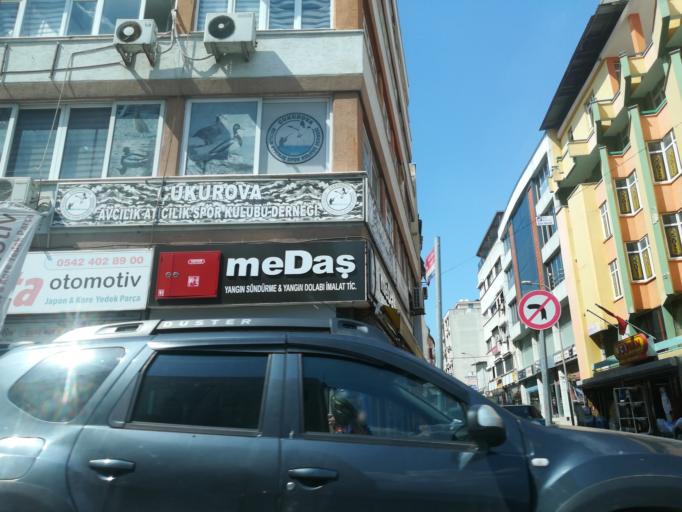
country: TR
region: Adana
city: Adana
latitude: 36.9851
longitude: 35.3297
